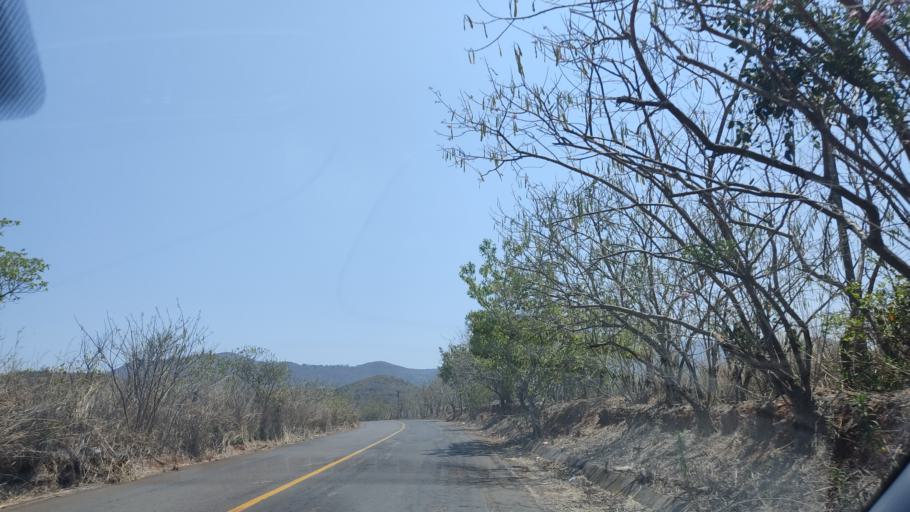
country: MX
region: Nayarit
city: Puga
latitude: 21.5795
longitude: -104.7728
